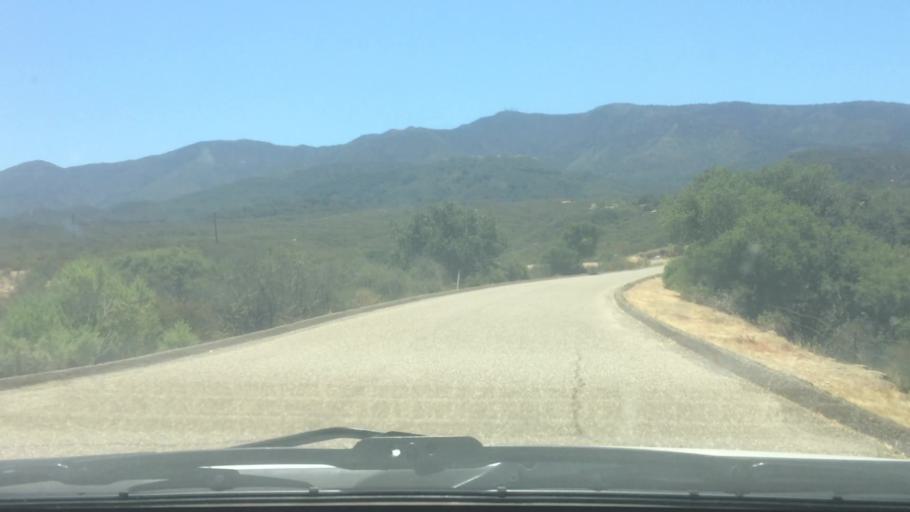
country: US
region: California
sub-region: Santa Barbara County
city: Santa Ynez
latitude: 34.5783
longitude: -119.9772
